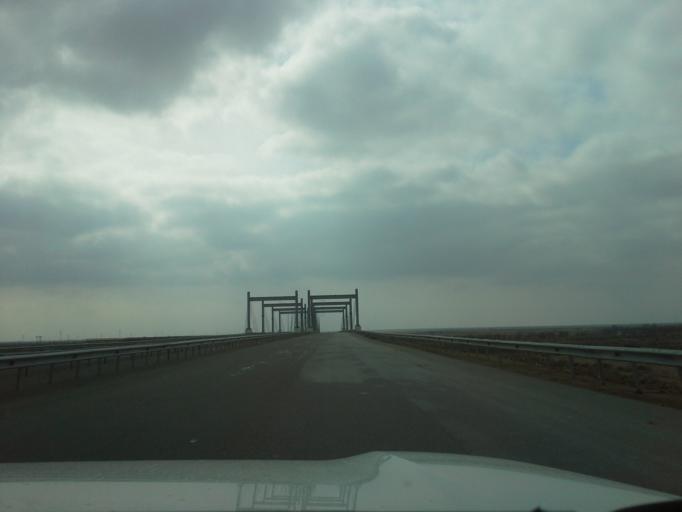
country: TM
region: Ahal
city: Tejen
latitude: 37.2336
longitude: 60.1545
